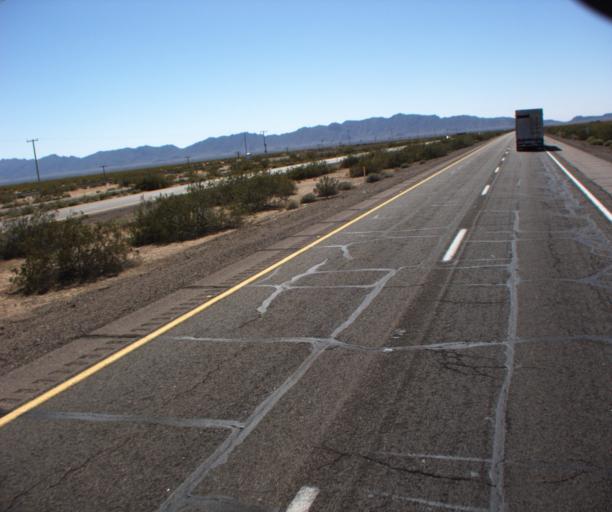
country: US
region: Arizona
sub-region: Yuma County
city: Wellton
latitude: 32.7716
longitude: -113.6075
